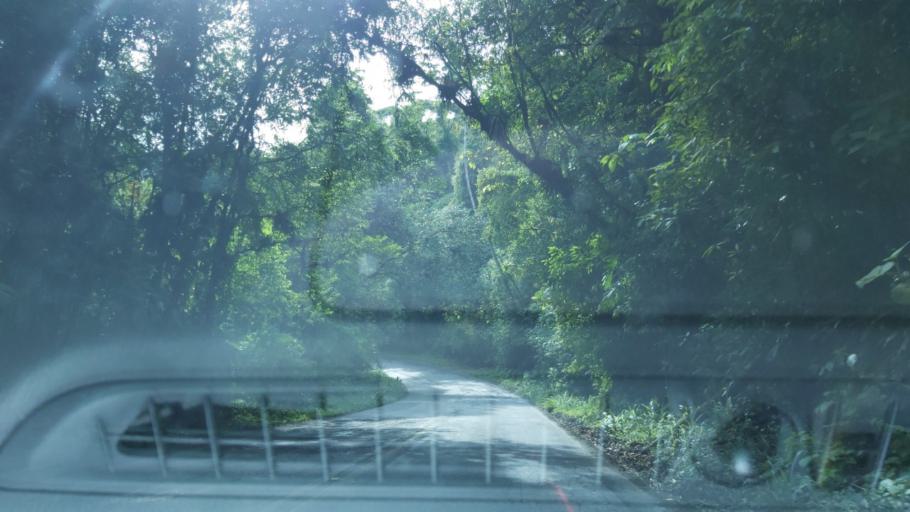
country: BR
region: Sao Paulo
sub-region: Miracatu
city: Miracatu
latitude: -24.0541
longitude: -47.5790
